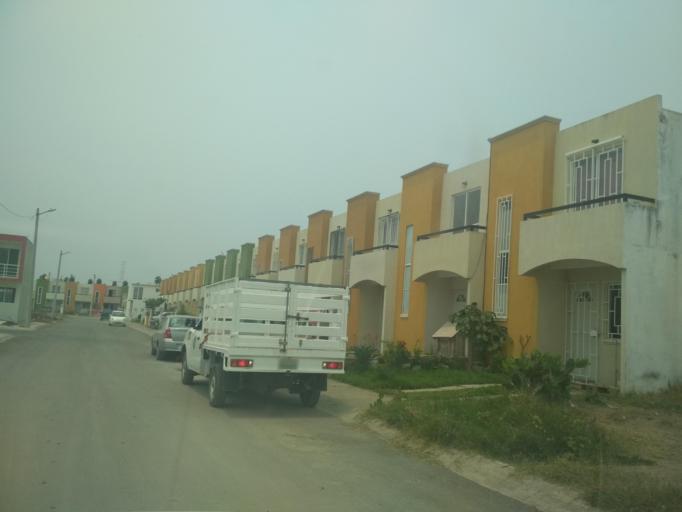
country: MX
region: Veracruz
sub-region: Veracruz
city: Las Amapolas
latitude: 19.1512
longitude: -96.2171
